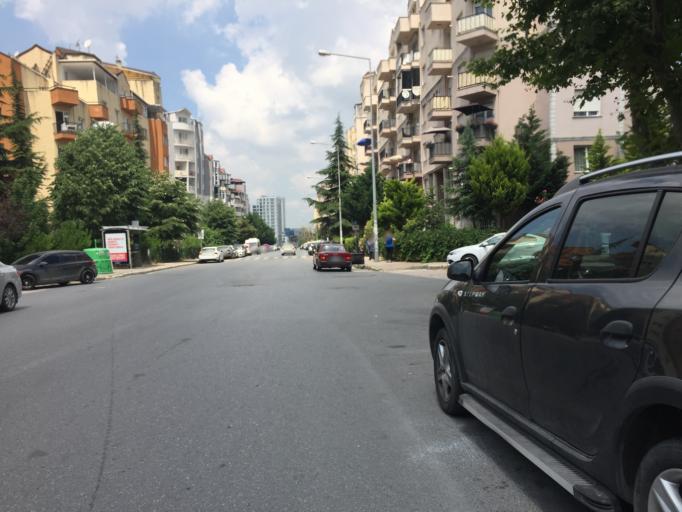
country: TR
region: Istanbul
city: Esenyurt
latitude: 41.0720
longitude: 28.6640
